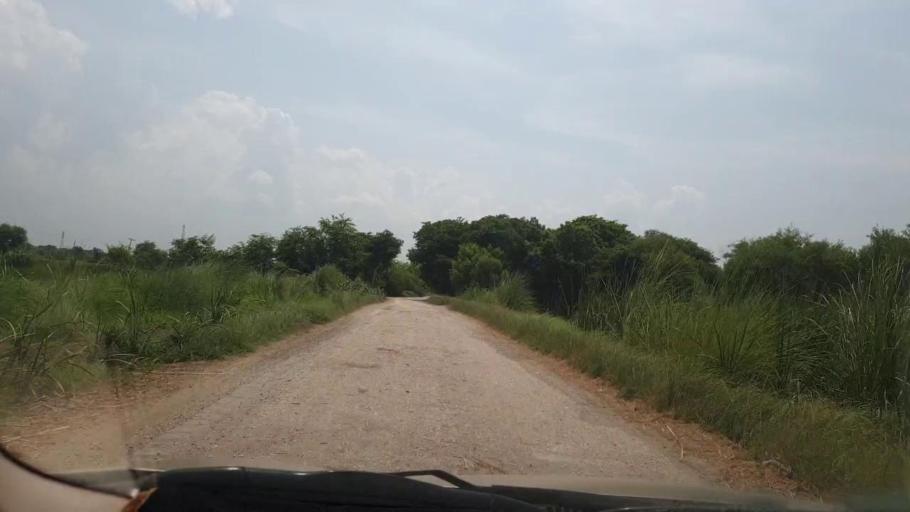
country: PK
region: Sindh
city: Larkana
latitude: 27.5874
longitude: 68.1186
